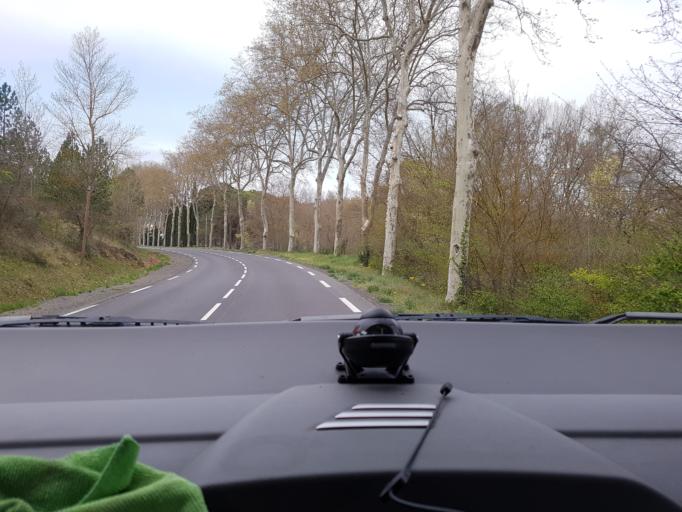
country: FR
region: Languedoc-Roussillon
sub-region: Departement de l'Aude
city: Couiza
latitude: 42.9394
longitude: 2.2430
